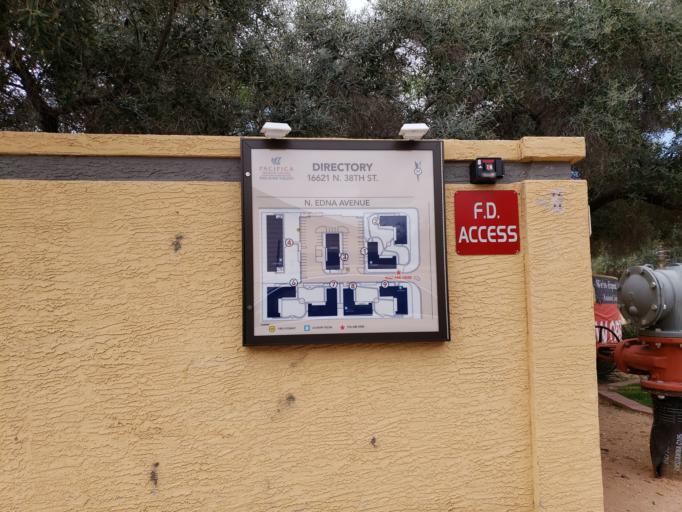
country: US
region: Arizona
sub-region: Maricopa County
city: Paradise Valley
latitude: 33.6377
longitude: -112.0002
